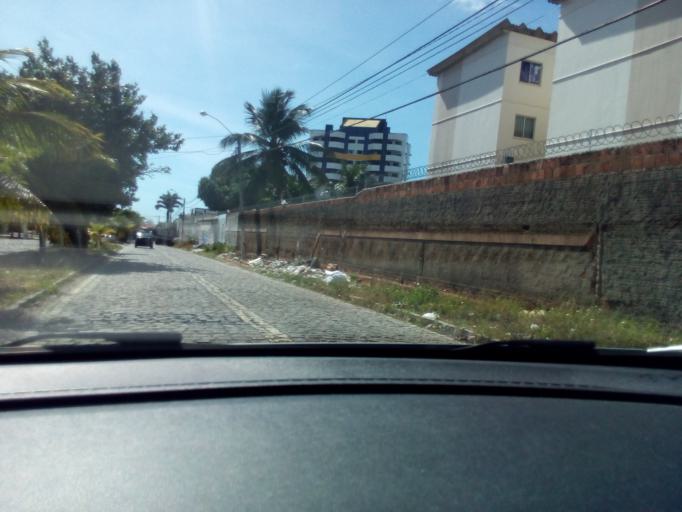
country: BR
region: Rio Grande do Norte
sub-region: Parnamirim
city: Parnamirim
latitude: -5.8872
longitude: -35.1979
